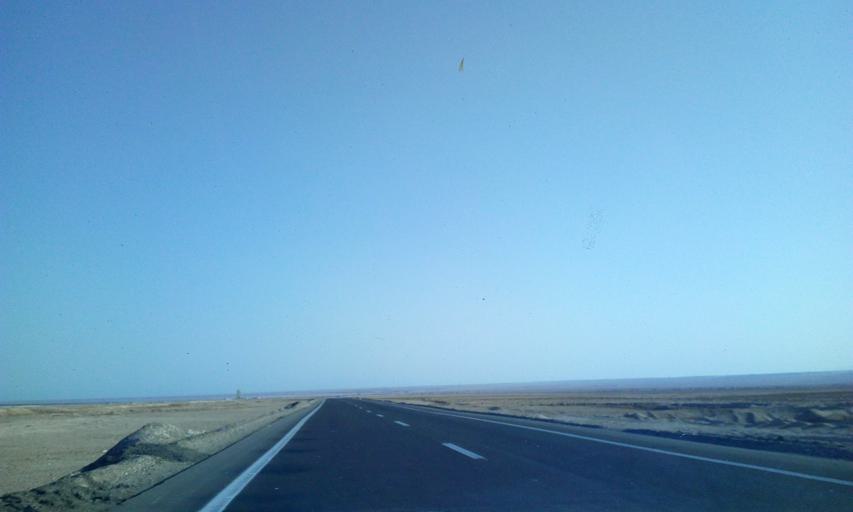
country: EG
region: South Sinai
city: Tor
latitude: 28.6076
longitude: 32.8618
